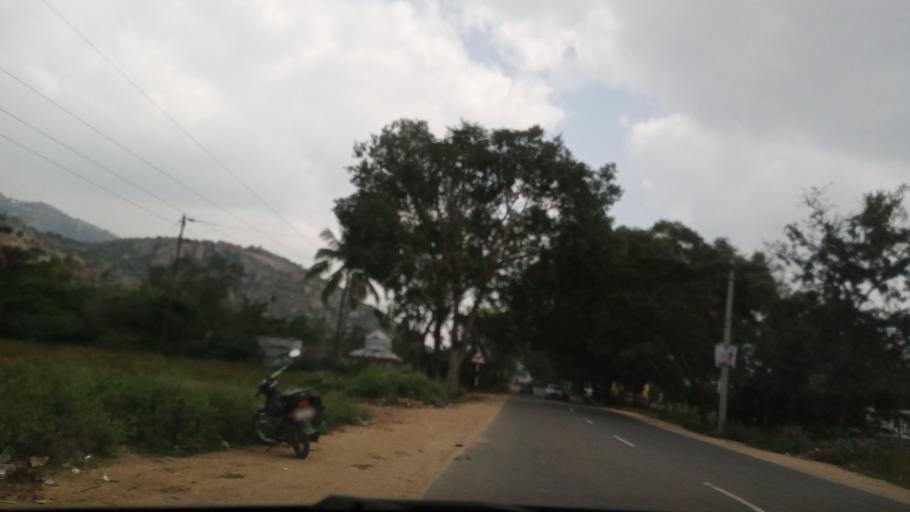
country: IN
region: Andhra Pradesh
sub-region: Chittoor
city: Madanapalle
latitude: 13.6426
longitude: 78.5699
